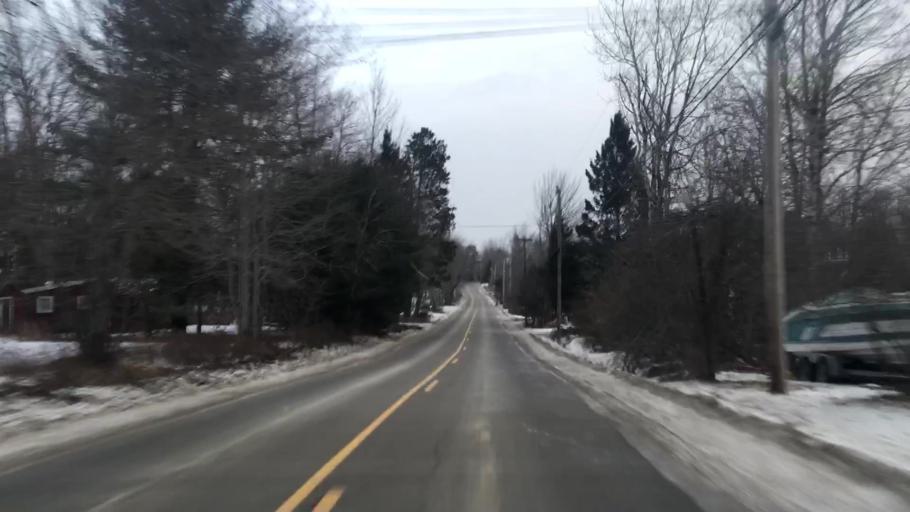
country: US
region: Maine
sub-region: Hancock County
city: Ellsworth
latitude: 44.6053
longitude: -68.3948
